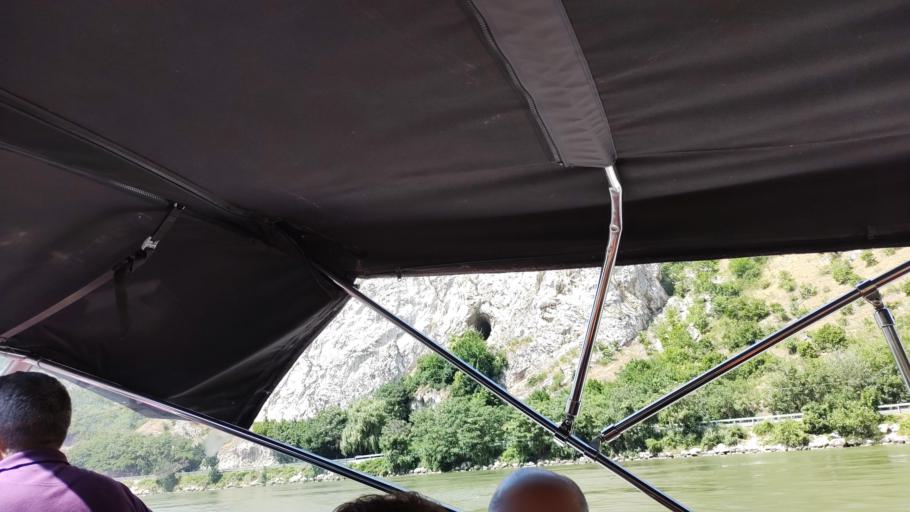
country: RO
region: Caras-Severin
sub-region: Comuna Pescari
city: Coronini
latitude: 44.6632
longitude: 21.6995
